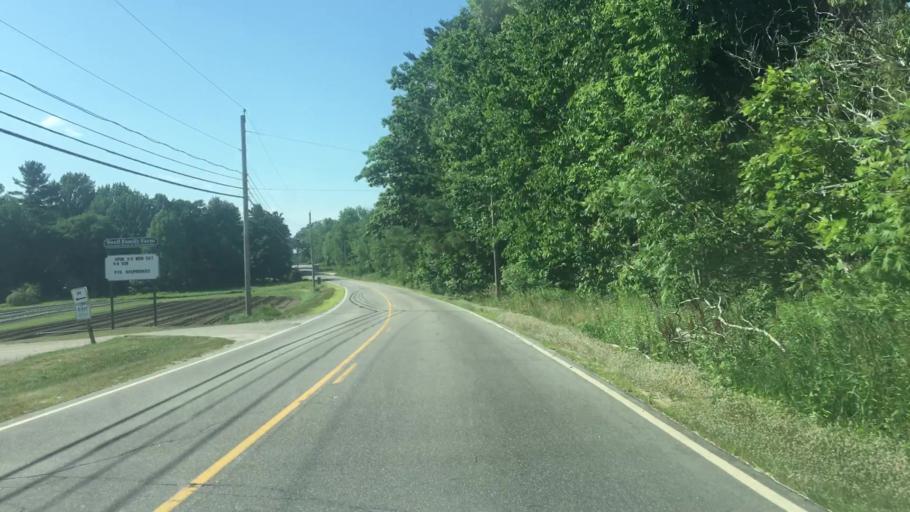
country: US
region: Maine
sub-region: York County
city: Buxton
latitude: 43.6198
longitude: -70.5437
